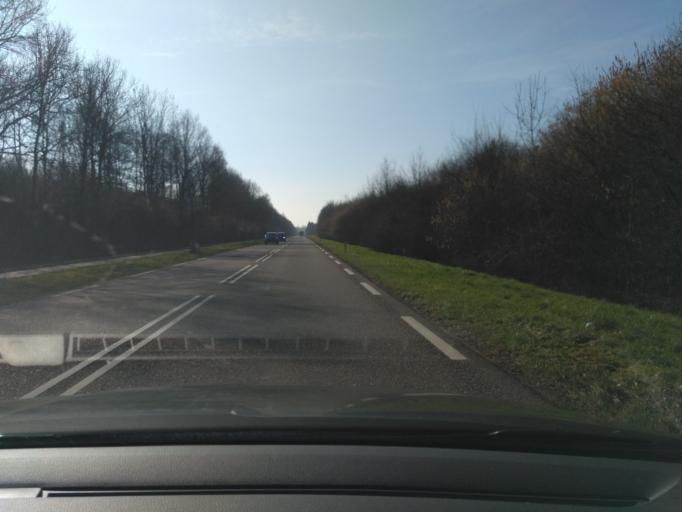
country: NL
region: Flevoland
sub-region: Gemeente Zeewolde
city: Zeewolde
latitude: 52.3076
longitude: 5.5162
